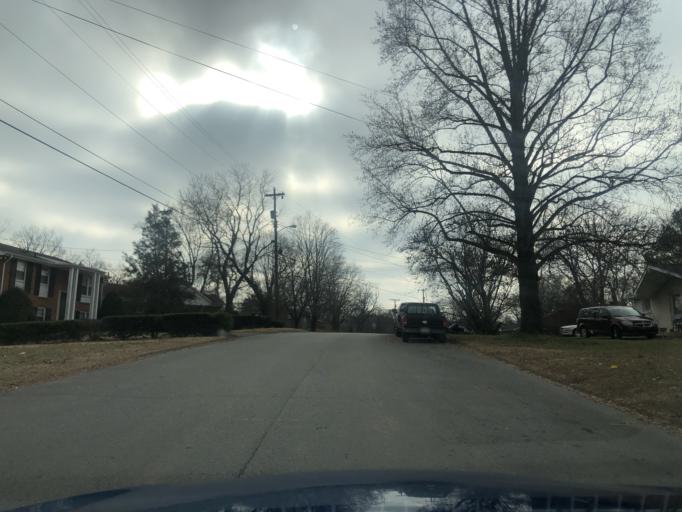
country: US
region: Tennessee
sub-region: Davidson County
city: Oak Hill
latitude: 36.0885
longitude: -86.7148
